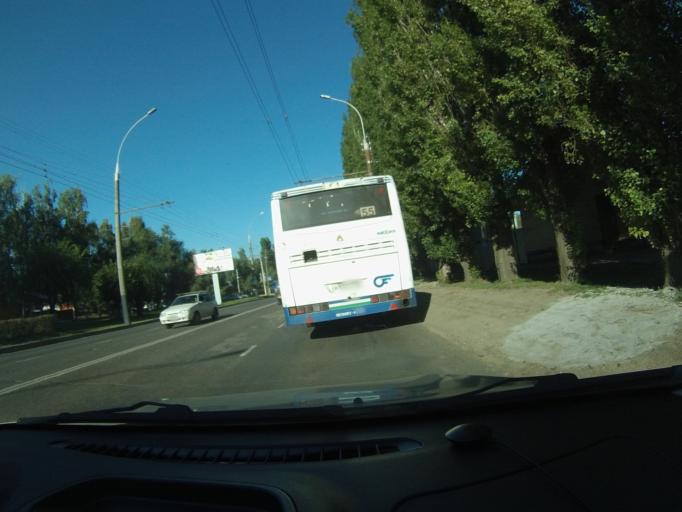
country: RU
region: Tambov
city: Tambov
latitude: 52.7524
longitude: 41.4231
